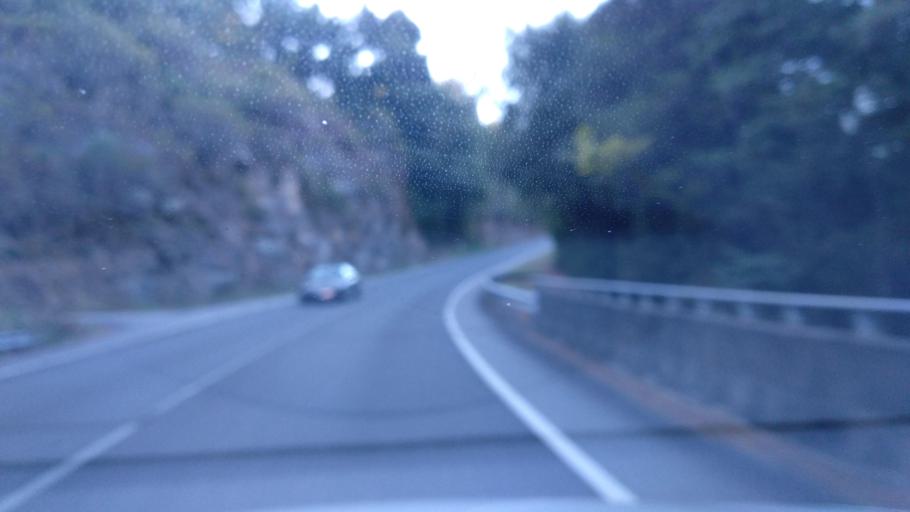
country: ES
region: Galicia
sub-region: Provincia de Pontevedra
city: Ponte Caldelas
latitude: 42.3407
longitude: -8.5571
